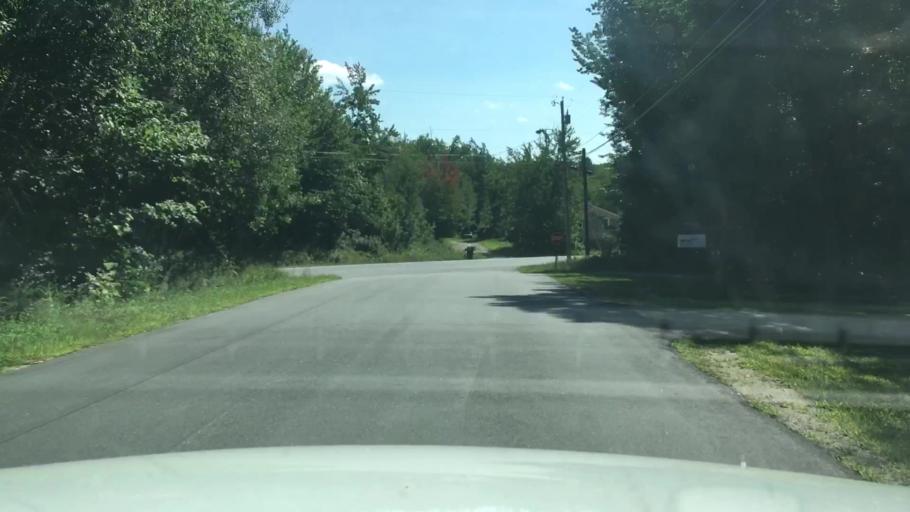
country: US
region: Maine
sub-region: Kennebec County
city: Monmouth
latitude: 44.2575
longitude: -70.0567
